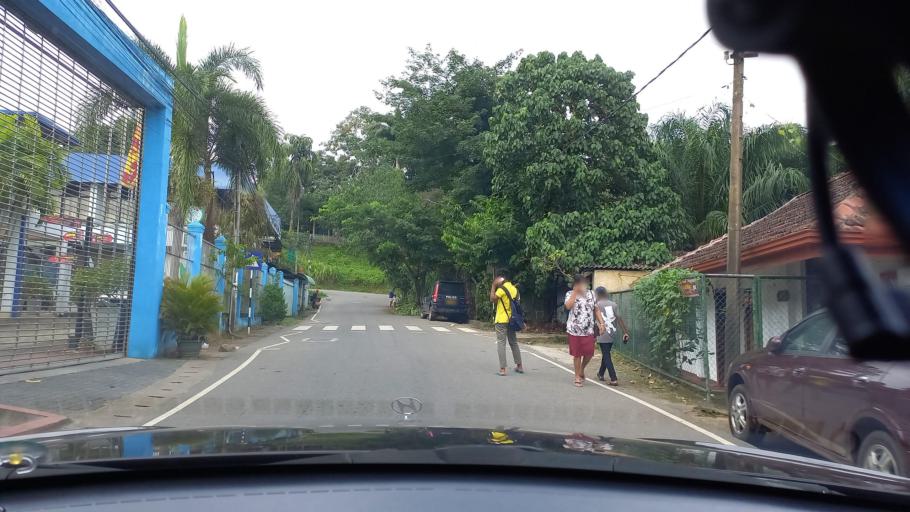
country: LK
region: Central
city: Kadugannawa
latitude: 7.2559
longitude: 80.3539
